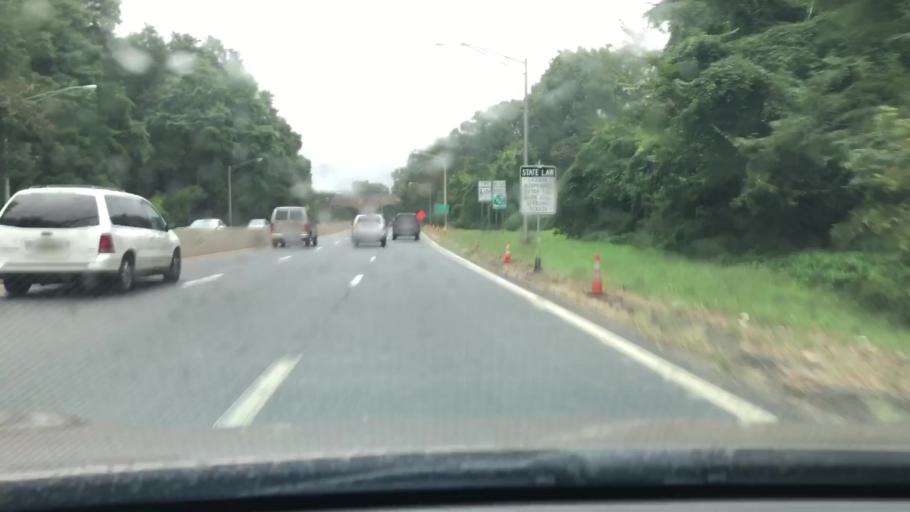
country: US
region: New York
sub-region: Westchester County
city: Yonkers
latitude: 40.9086
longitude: -73.8858
